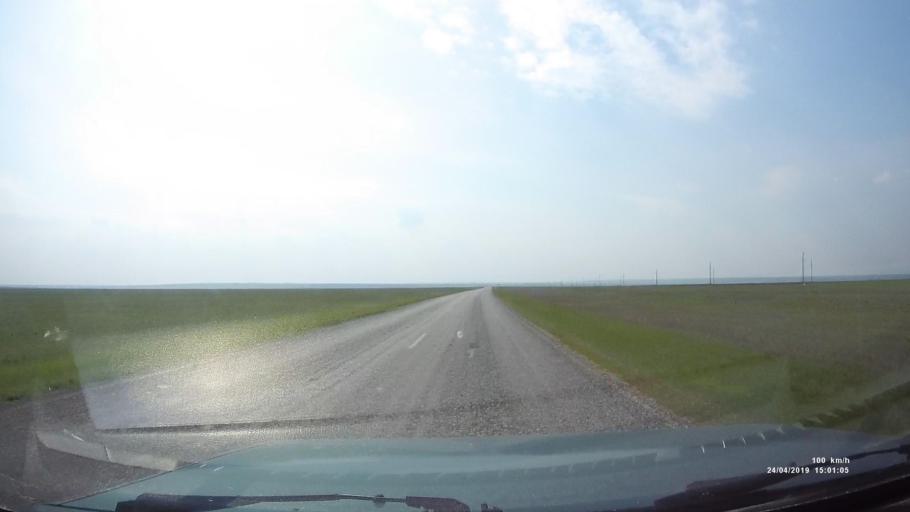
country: RU
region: Rostov
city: Remontnoye
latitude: 46.5655
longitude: 43.5416
